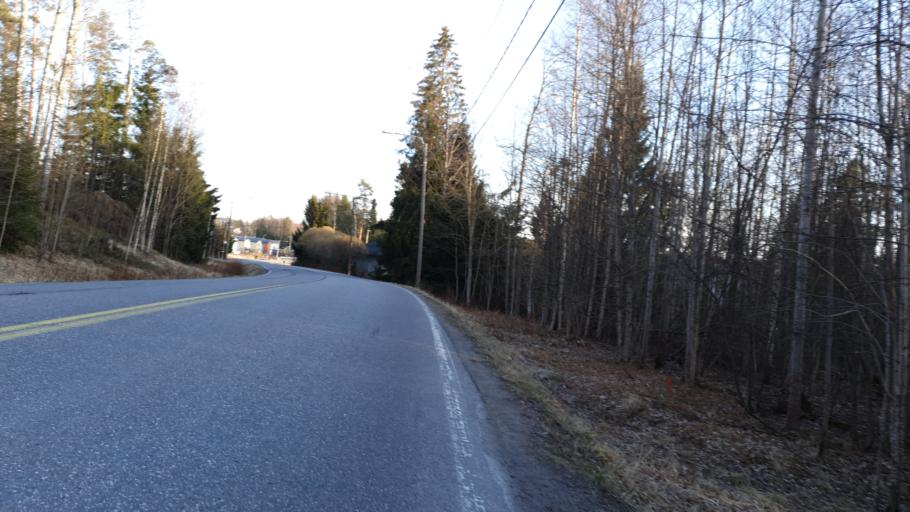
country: FI
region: Uusimaa
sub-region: Helsinki
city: Kilo
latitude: 60.3306
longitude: 24.8344
